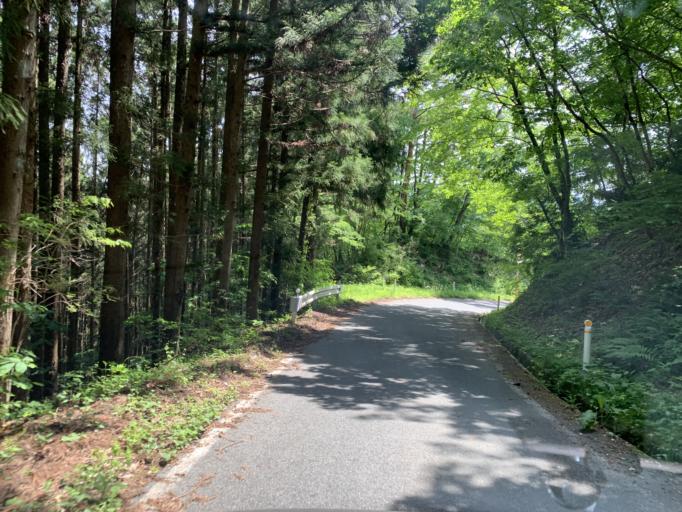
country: JP
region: Iwate
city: Ichinoseki
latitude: 38.9664
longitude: 141.2322
